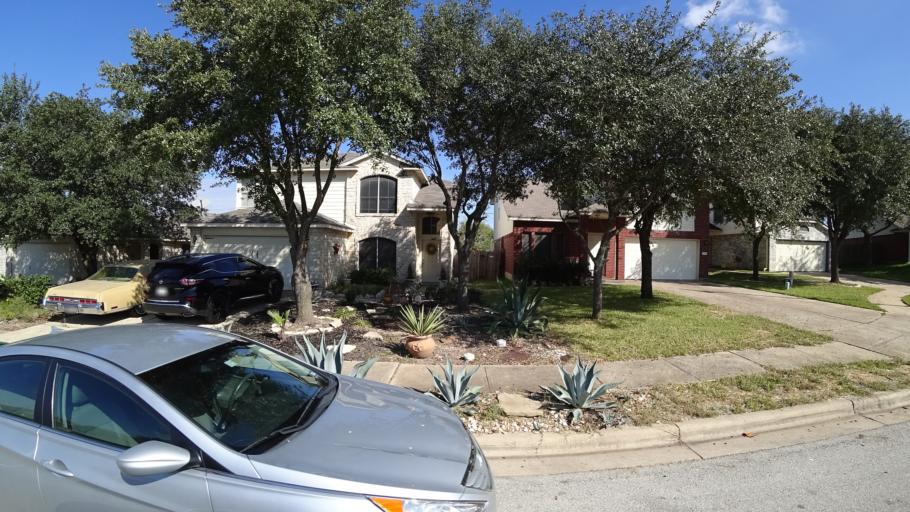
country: US
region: Texas
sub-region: Travis County
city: Windemere
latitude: 30.4471
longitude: -97.6553
